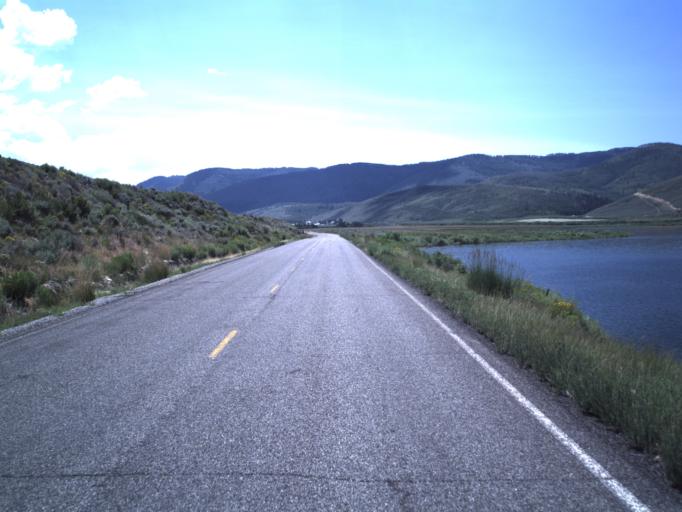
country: US
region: Utah
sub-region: Carbon County
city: Helper
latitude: 39.7544
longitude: -111.1485
